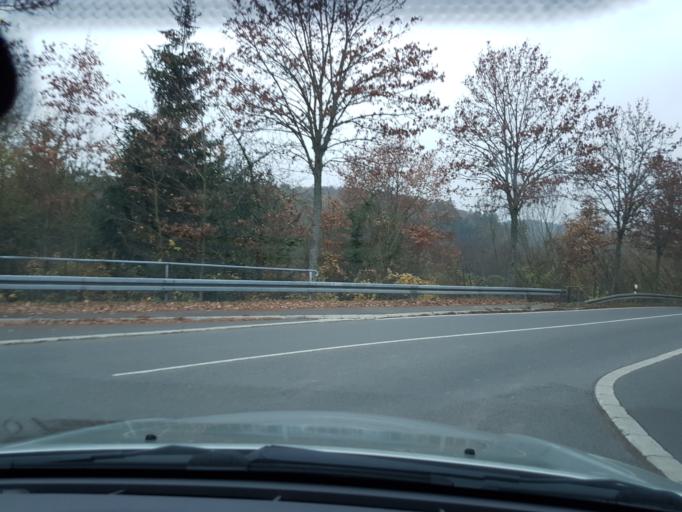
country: DE
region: Hesse
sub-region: Regierungsbezirk Darmstadt
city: Kiedrich
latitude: 50.0389
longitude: 8.0551
